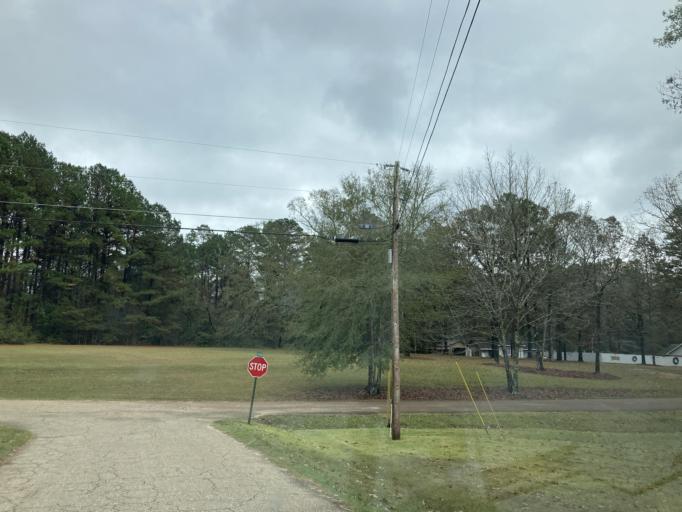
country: US
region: Mississippi
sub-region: Lamar County
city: West Hattiesburg
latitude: 31.2907
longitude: -89.4746
